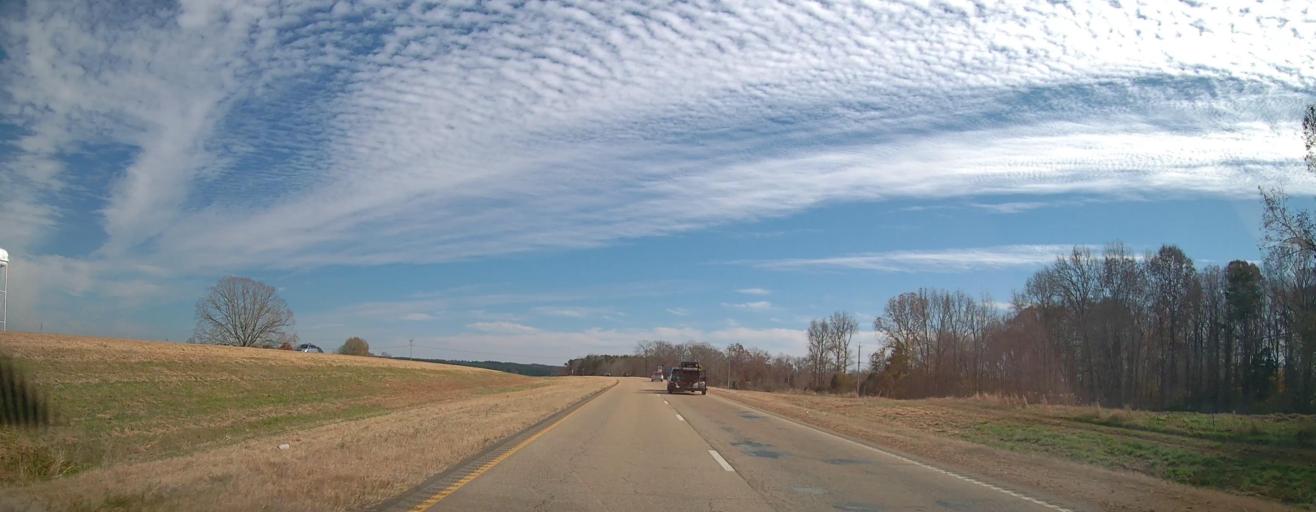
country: US
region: Mississippi
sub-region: Tippah County
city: Ripley
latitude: 34.9469
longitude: -88.8042
